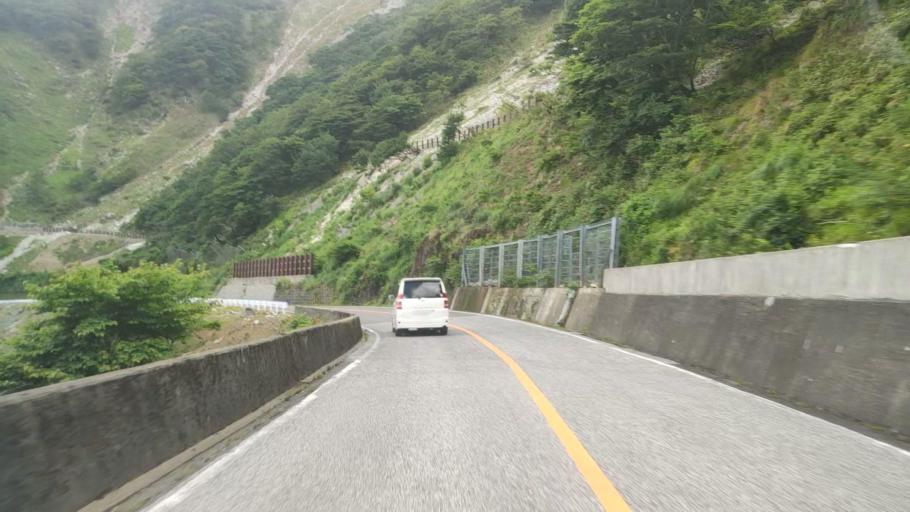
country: JP
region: Gifu
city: Tarui
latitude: 35.4239
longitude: 136.4174
